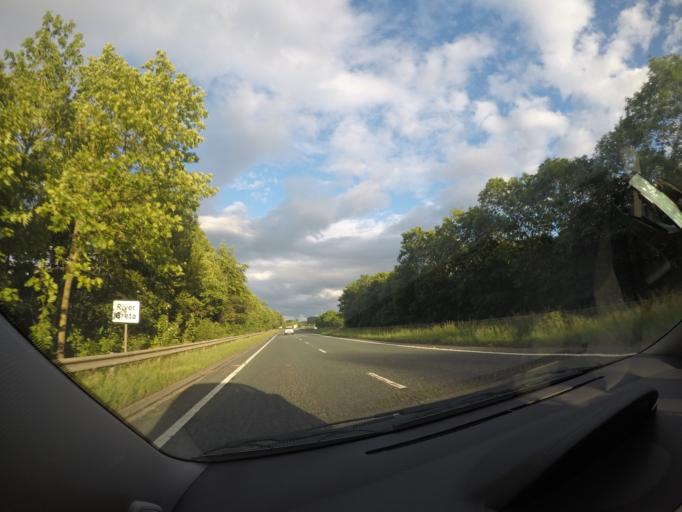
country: GB
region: England
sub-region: County Durham
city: Rokeby
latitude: 54.5161
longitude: -1.8690
